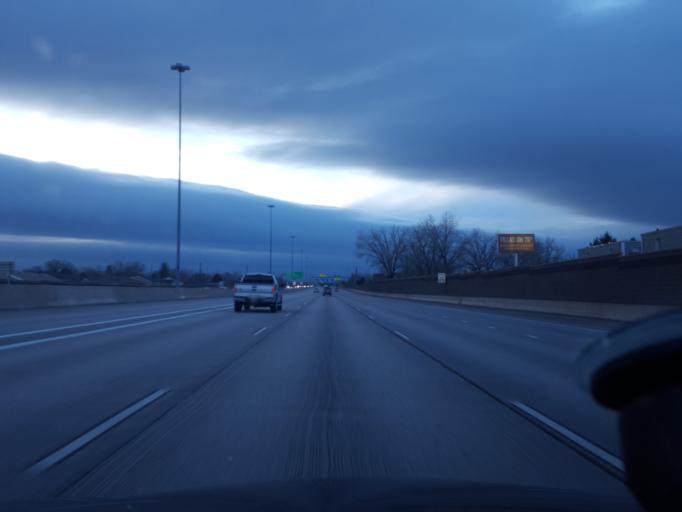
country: US
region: Colorado
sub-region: Adams County
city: Twin Lakes
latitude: 39.8322
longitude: -105.0111
